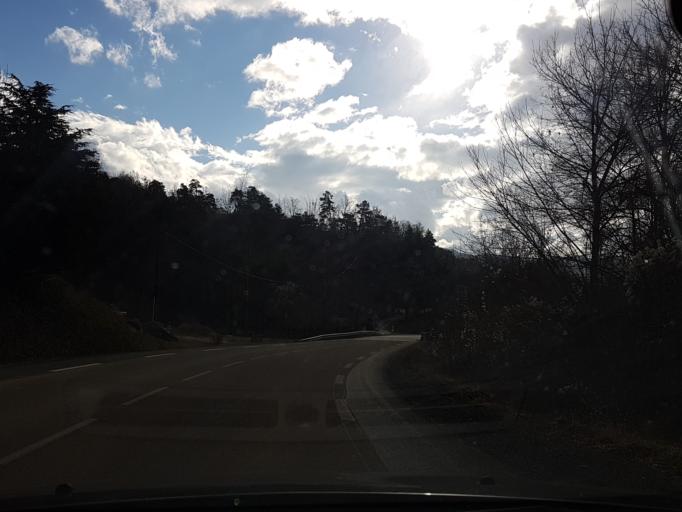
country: FR
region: Provence-Alpes-Cote d'Azur
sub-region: Departement des Hautes-Alpes
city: Tallard
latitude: 44.5105
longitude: 6.0796
